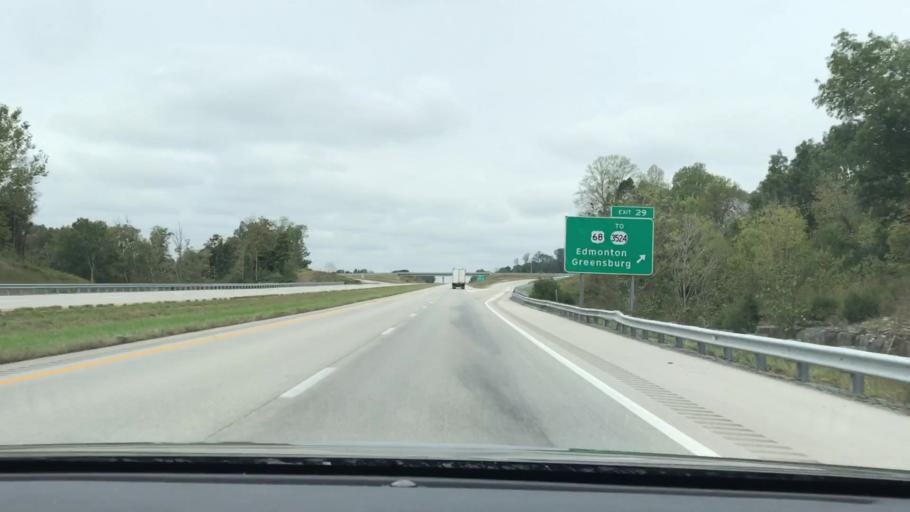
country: US
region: Kentucky
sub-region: Metcalfe County
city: Edmonton
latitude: 37.0026
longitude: -85.6091
